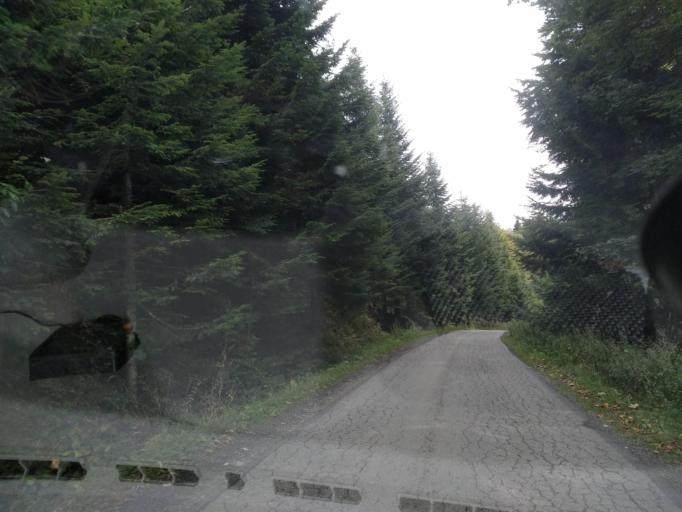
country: PL
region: Lesser Poland Voivodeship
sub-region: Powiat gorlicki
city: Sekowa
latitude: 49.5450
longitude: 21.2328
